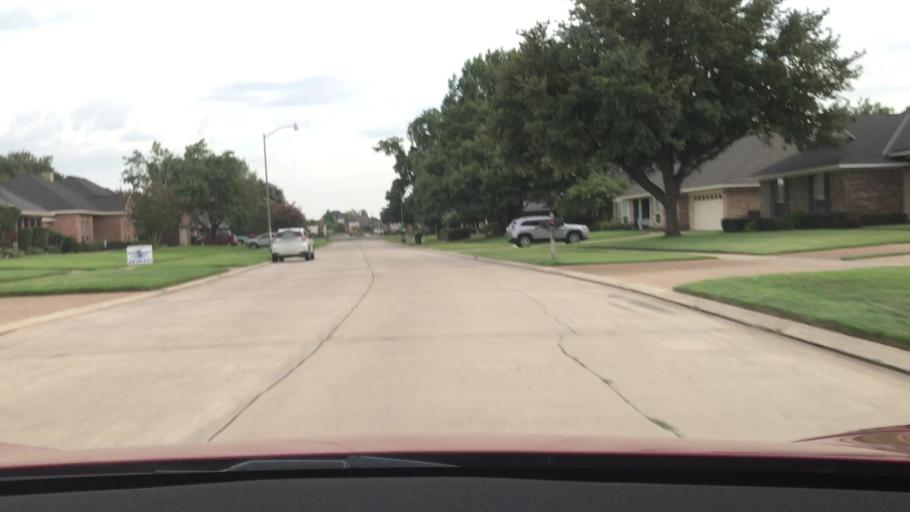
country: US
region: Louisiana
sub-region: Bossier Parish
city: Bossier City
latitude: 32.4549
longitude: -93.6707
